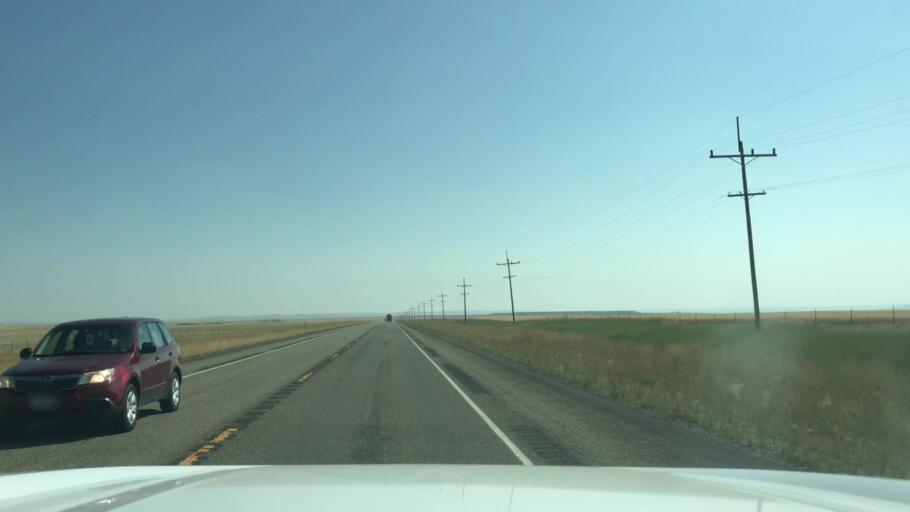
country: US
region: Montana
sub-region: Wheatland County
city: Harlowton
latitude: 46.5099
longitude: -109.7661
